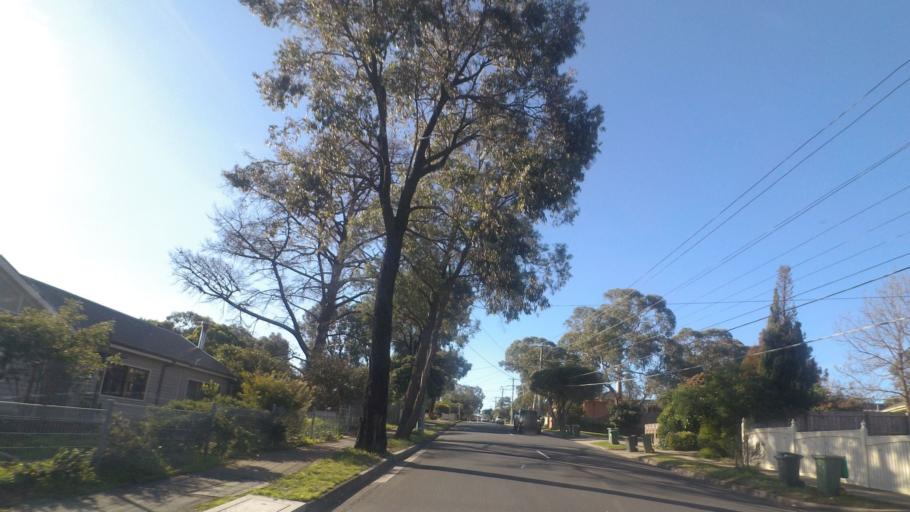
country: AU
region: Victoria
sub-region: Banyule
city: Montmorency
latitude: -37.7191
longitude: 145.1154
